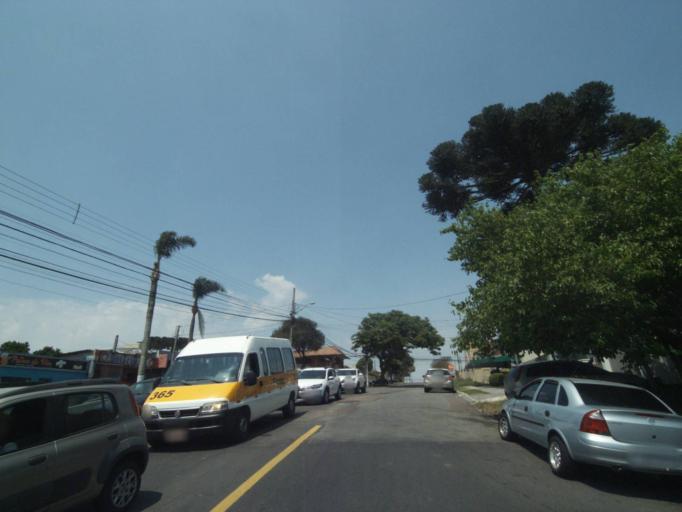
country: BR
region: Parana
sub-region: Curitiba
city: Curitiba
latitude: -25.4776
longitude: -49.3097
